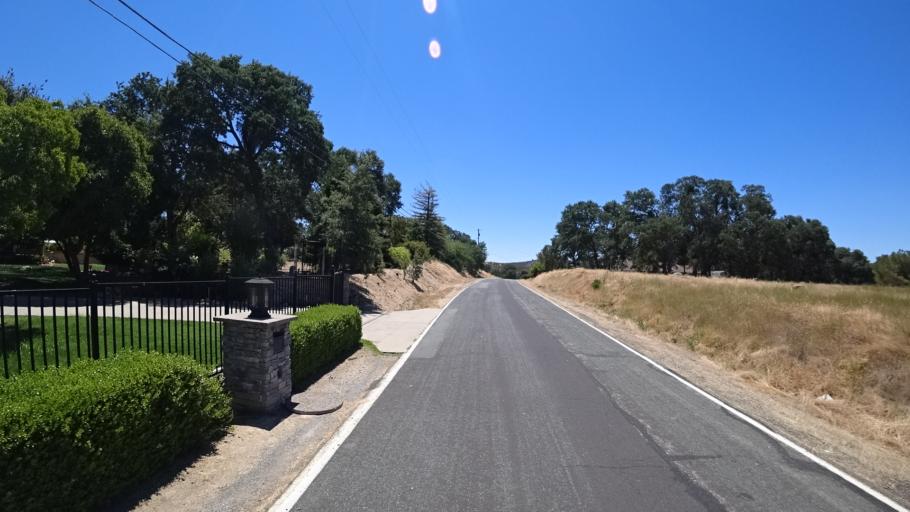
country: US
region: California
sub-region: Calaveras County
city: Rancho Calaveras
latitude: 38.1383
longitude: -120.8365
